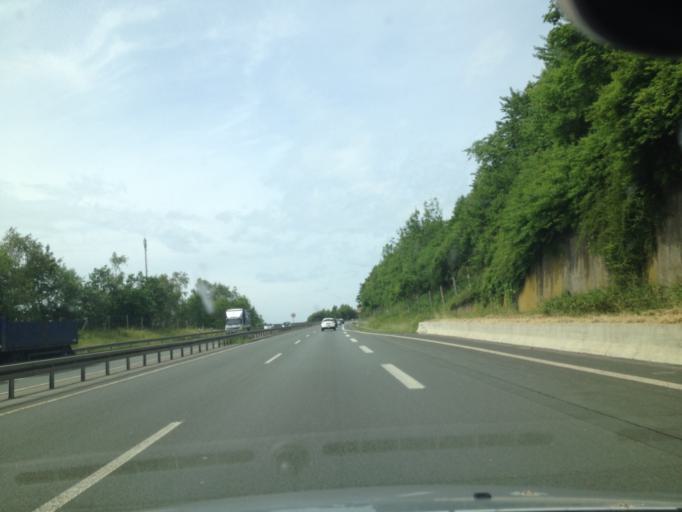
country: DE
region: North Rhine-Westphalia
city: Kreuztal
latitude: 50.9373
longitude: 8.0083
